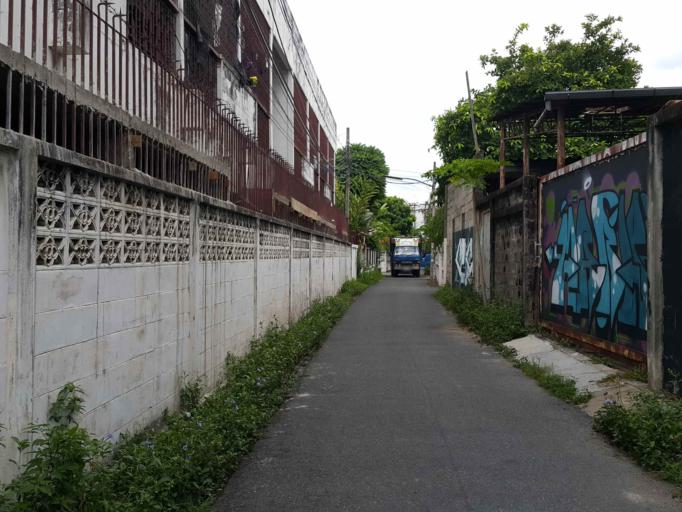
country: TH
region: Chiang Mai
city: Chiang Mai
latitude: 18.7930
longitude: 98.9915
